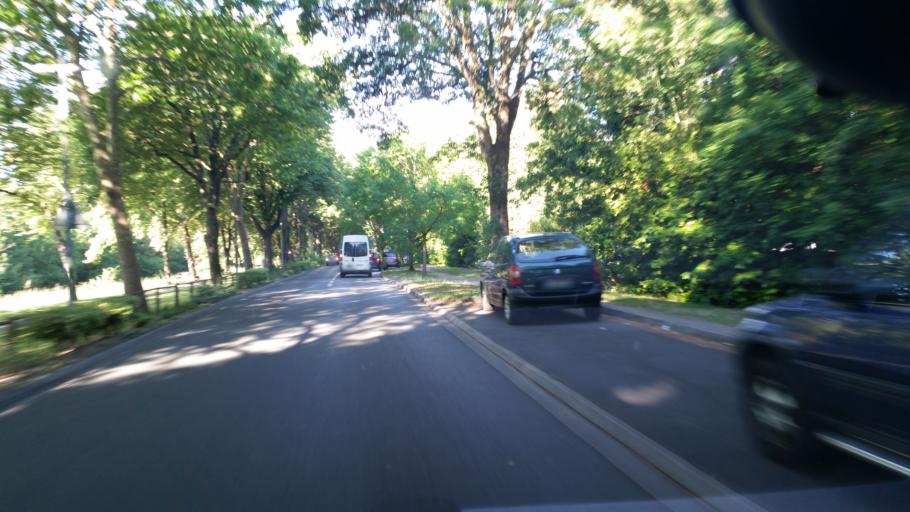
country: FR
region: Poitou-Charentes
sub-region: Departement de la Charente-Maritime
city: Perigny
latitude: 46.1655
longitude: -1.1125
